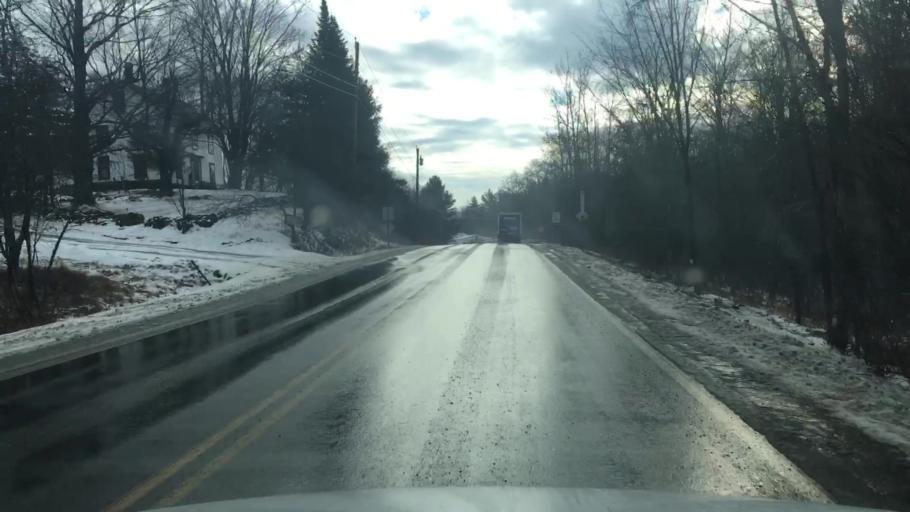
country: US
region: Maine
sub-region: Penobscot County
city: Brewer
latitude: 44.7615
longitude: -68.7750
